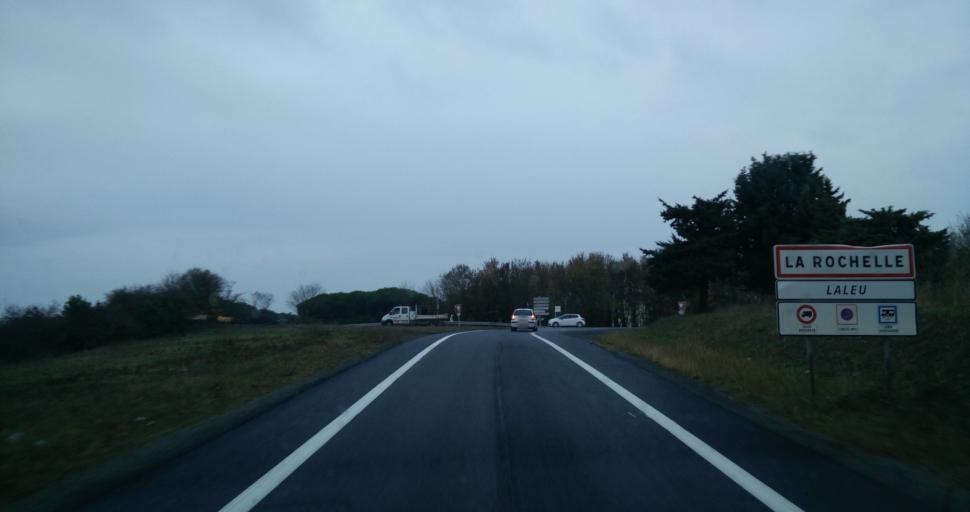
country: FR
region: Poitou-Charentes
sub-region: Departement de la Charente-Maritime
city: Nieul-sur-Mer
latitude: 46.1730
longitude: -1.1980
